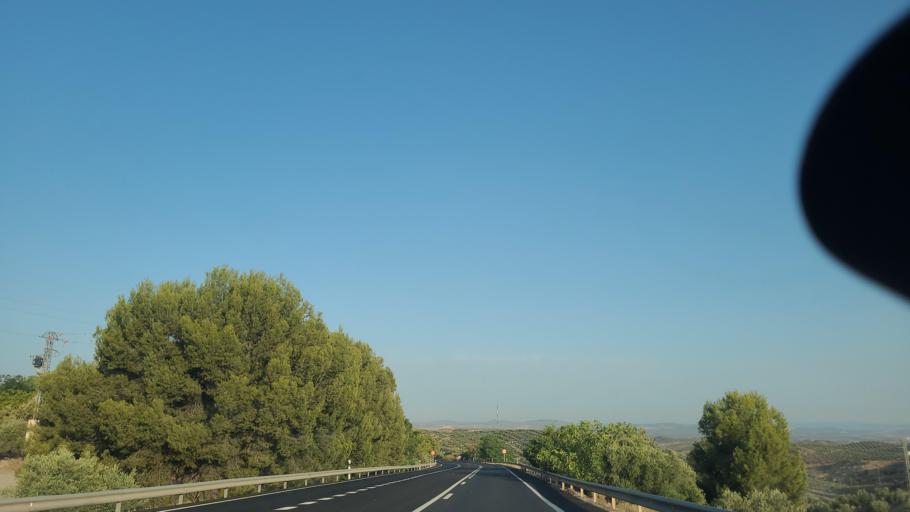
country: ES
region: Andalusia
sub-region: Provincia de Jaen
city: Mancha Real
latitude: 37.8044
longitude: -3.6491
